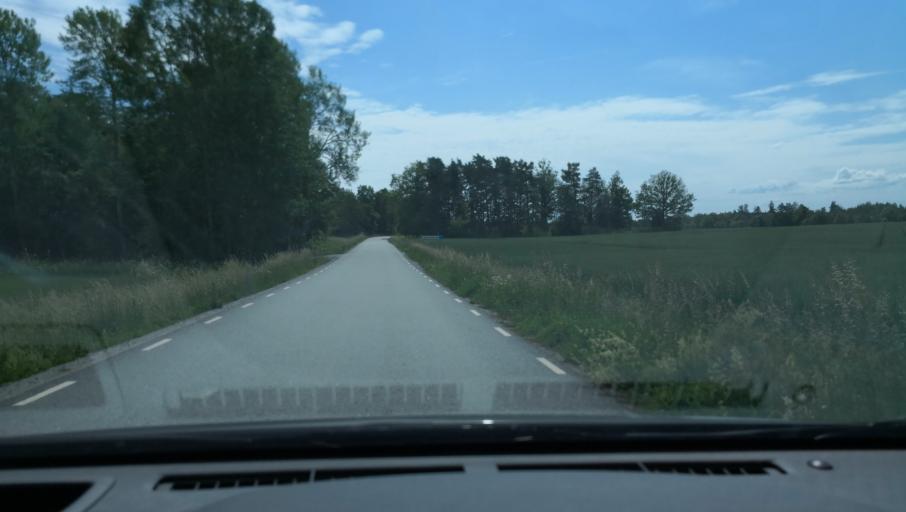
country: SE
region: Uppsala
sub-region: Habo Kommun
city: Balsta
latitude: 59.6788
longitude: 17.4669
